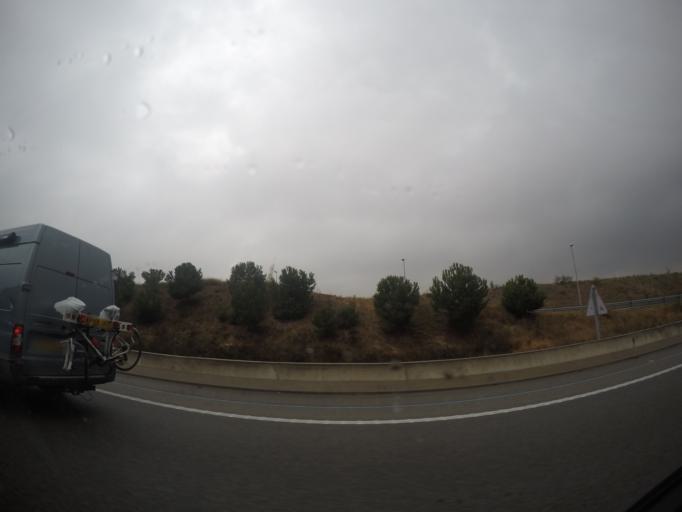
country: ES
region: Catalonia
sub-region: Provincia de Barcelona
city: Vilafranca del Penedes
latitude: 41.3378
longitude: 1.7163
